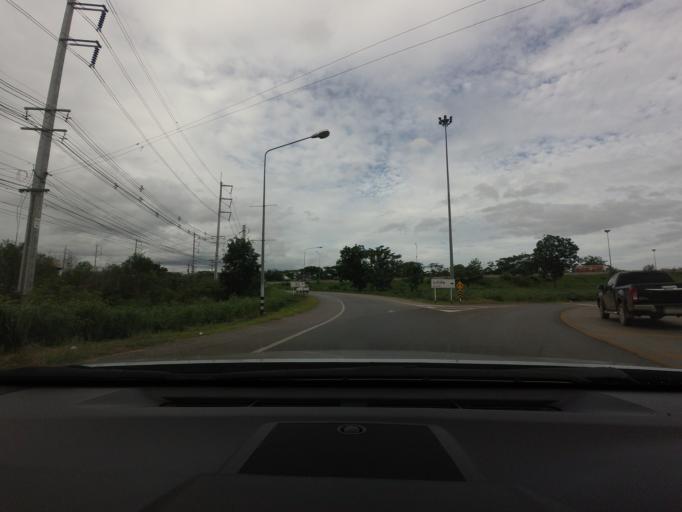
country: TH
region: Prachuap Khiri Khan
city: Hua Hin
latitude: 12.5767
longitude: 99.8658
